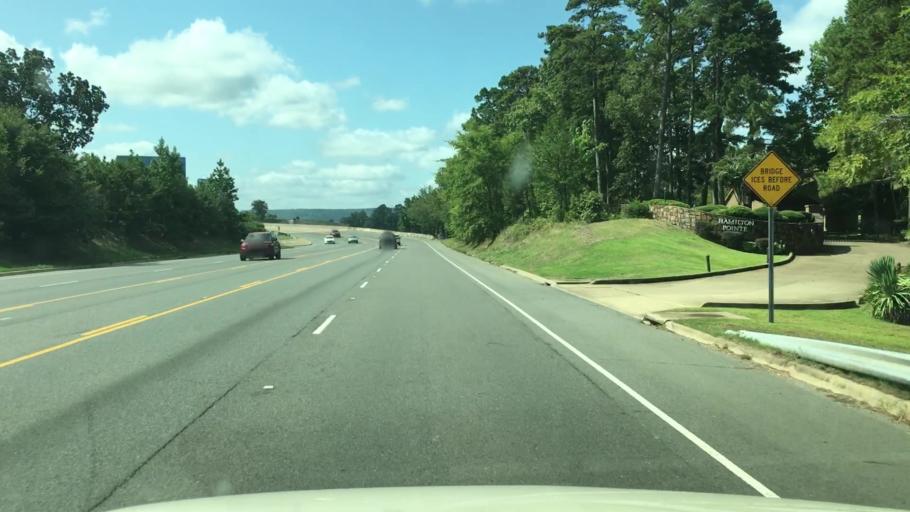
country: US
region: Arkansas
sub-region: Garland County
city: Lake Hamilton
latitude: 34.4366
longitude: -93.0886
